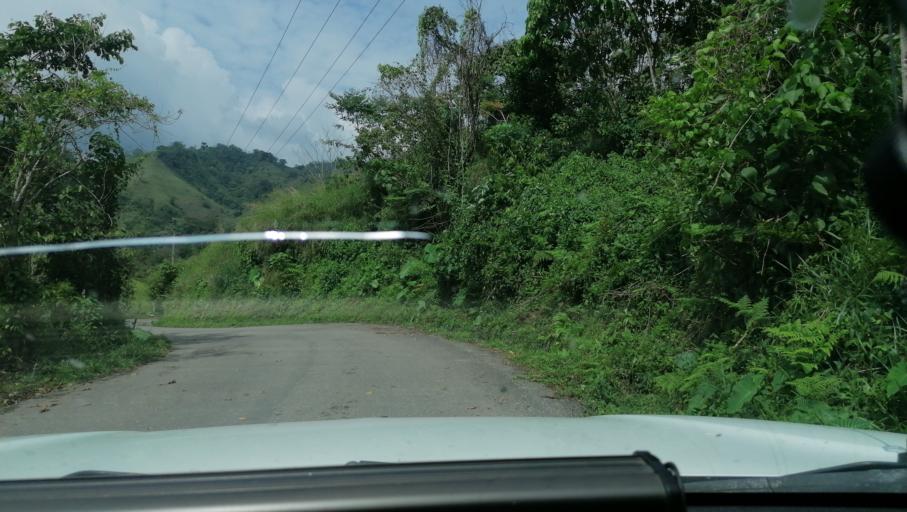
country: MX
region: Chiapas
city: Ocotepec
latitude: 17.3223
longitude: -93.1683
